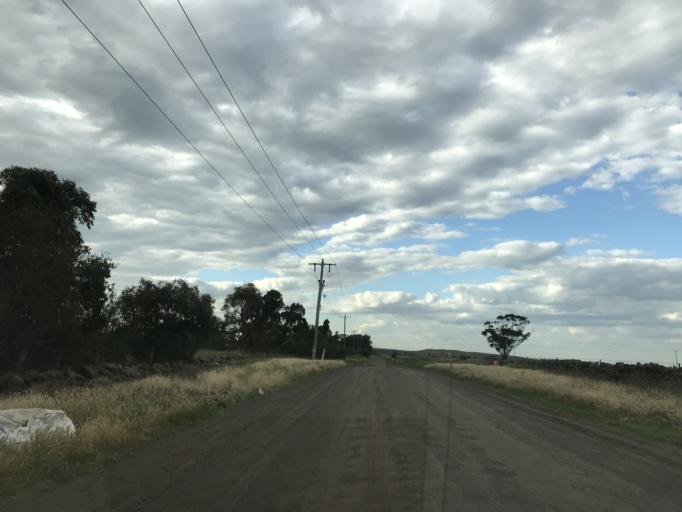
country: AU
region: Victoria
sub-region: Wyndham
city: Truganina
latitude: -37.8108
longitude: 144.7230
